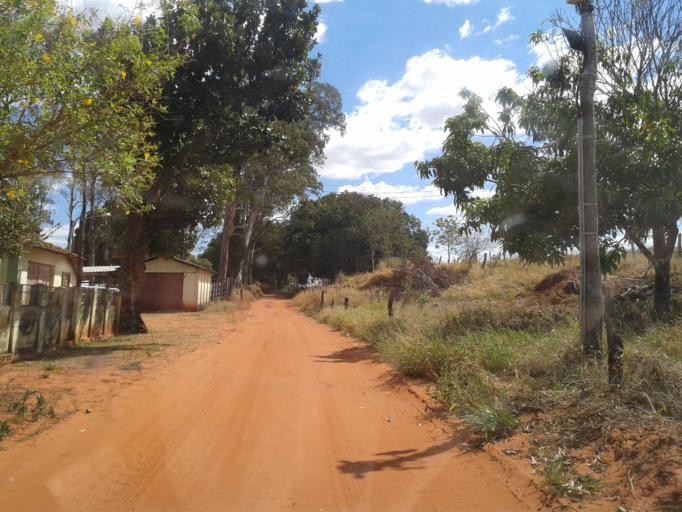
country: BR
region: Minas Gerais
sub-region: Centralina
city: Centralina
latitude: -18.7770
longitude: -49.0888
